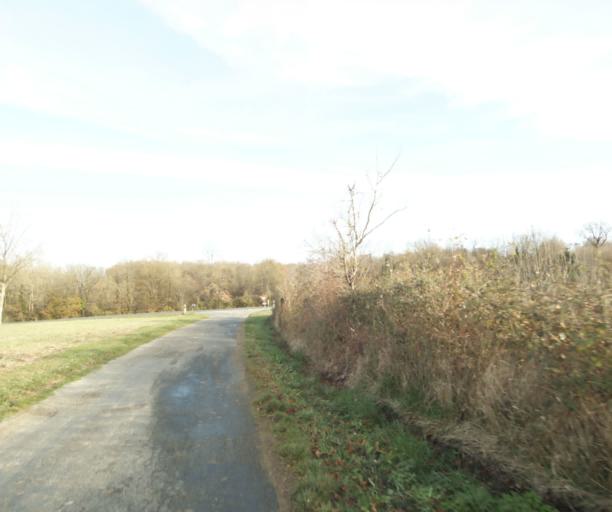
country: FR
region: Poitou-Charentes
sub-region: Departement de la Charente-Maritime
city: Saint-Hilaire-de-Villefranche
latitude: 45.8256
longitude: -0.5431
